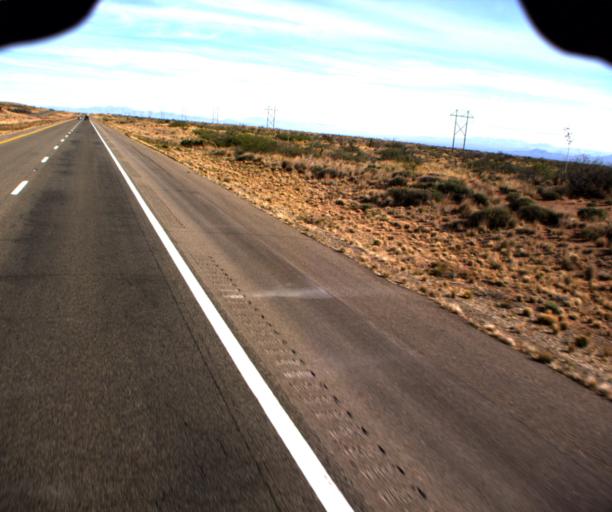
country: US
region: Arizona
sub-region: Graham County
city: Swift Trail Junction
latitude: 32.4777
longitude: -109.6728
